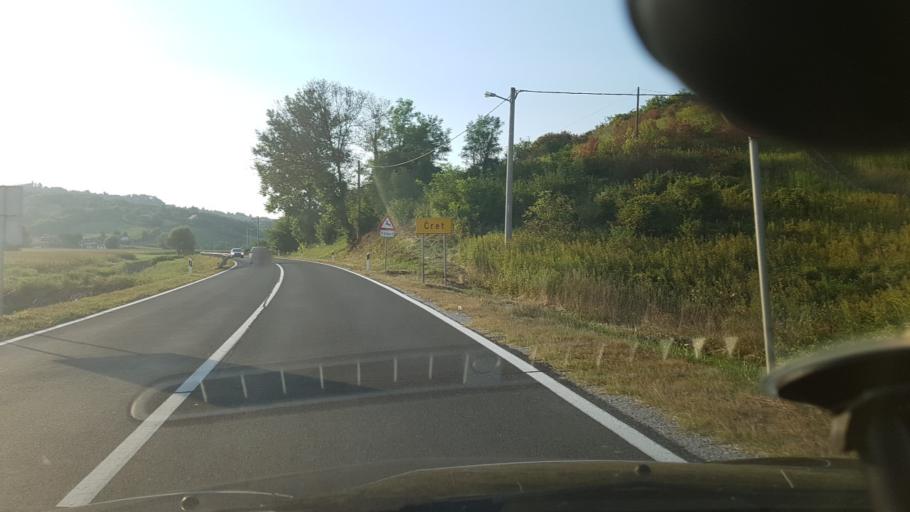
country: HR
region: Krapinsko-Zagorska
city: Pregrada
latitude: 46.1130
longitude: 15.8114
